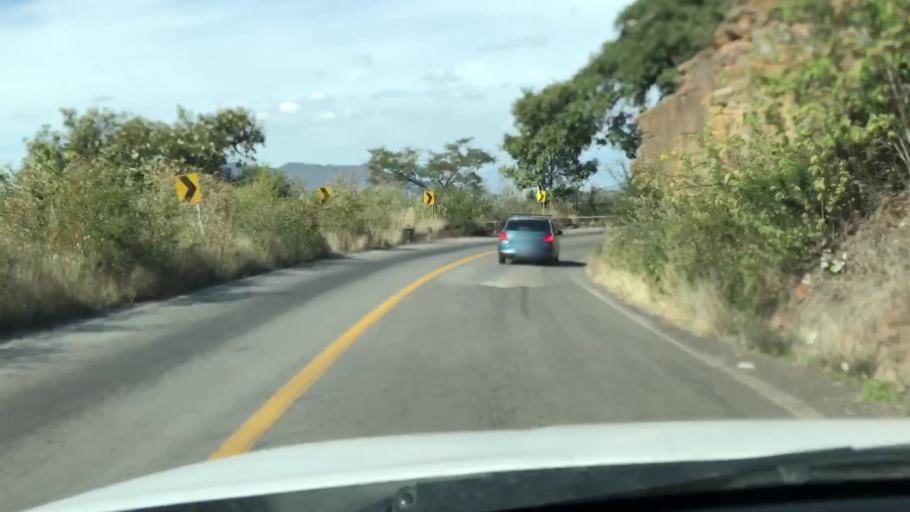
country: MX
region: Jalisco
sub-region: Zacoalco de Torres
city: Barranca de Otates (Barranca de Otatan)
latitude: 20.2009
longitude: -103.6961
